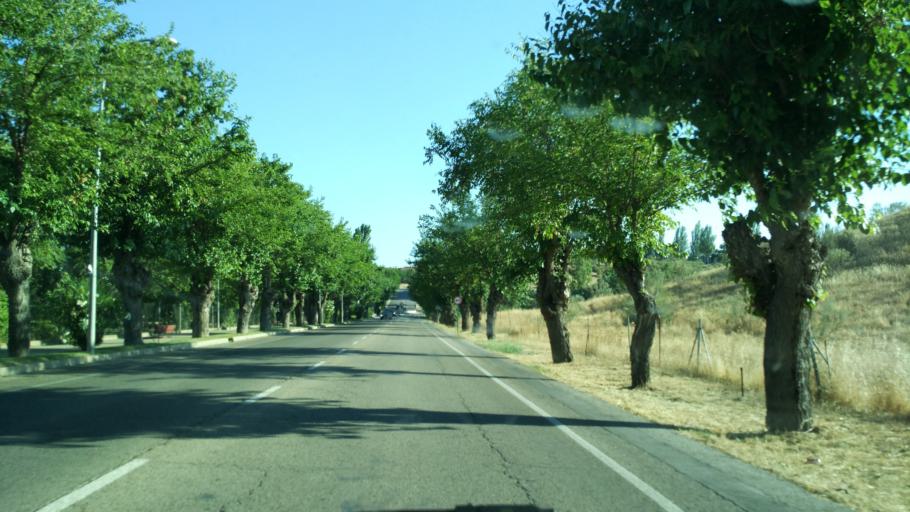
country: ES
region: Madrid
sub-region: Provincia de Madrid
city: San Agustin de Guadalix
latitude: 40.6878
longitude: -3.6106
